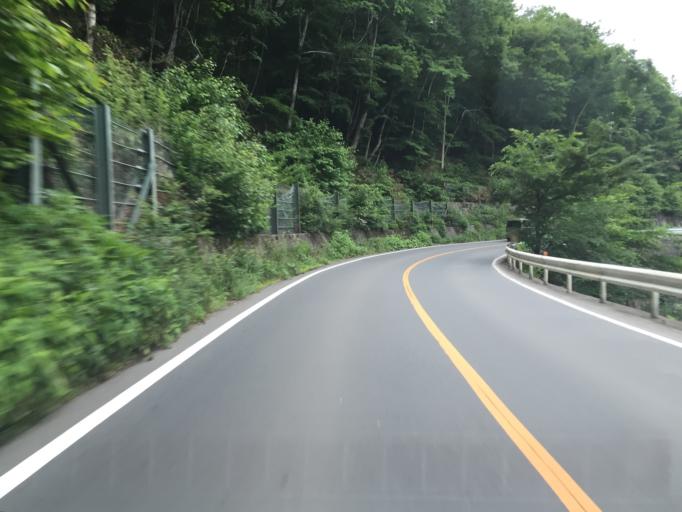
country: JP
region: Miyagi
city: Marumori
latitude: 37.7685
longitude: 140.7906
